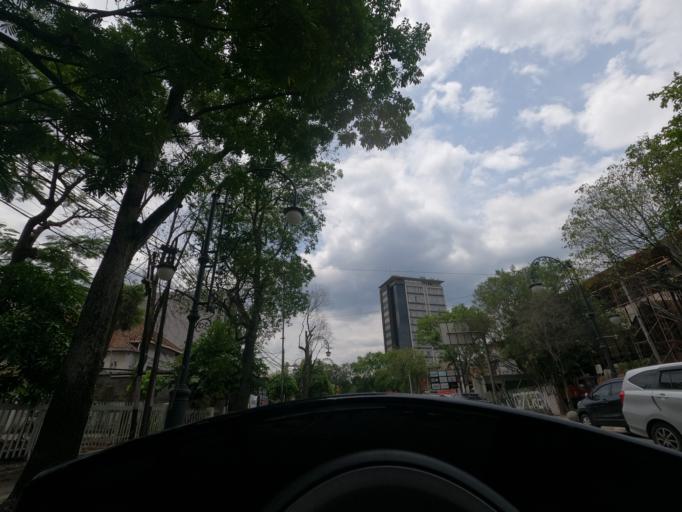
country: ID
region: West Java
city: Bandung
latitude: -6.9146
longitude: 107.6295
